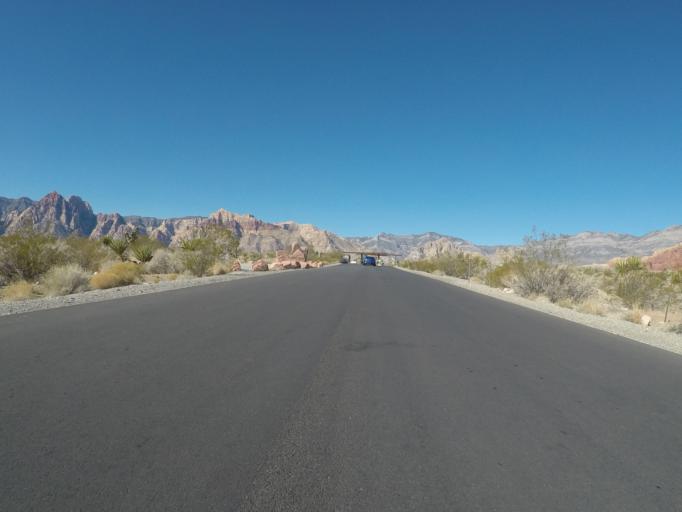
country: US
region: Nevada
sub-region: Clark County
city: Summerlin South
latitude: 36.1320
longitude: -115.4220
